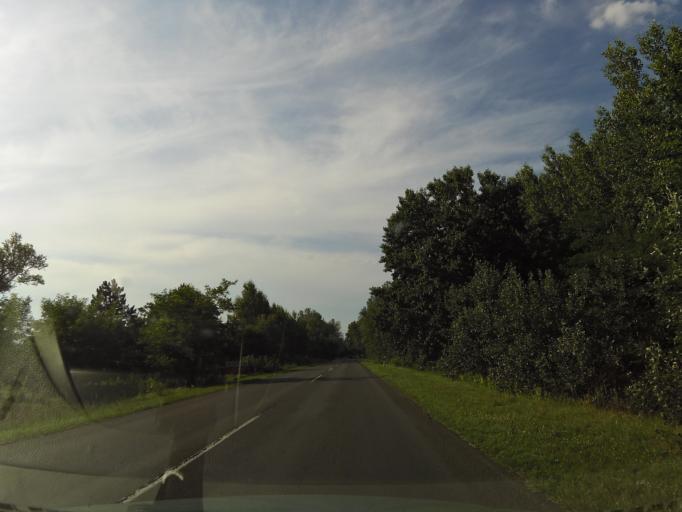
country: HU
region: Csongrad
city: Balastya
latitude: 46.3988
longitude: 20.0264
